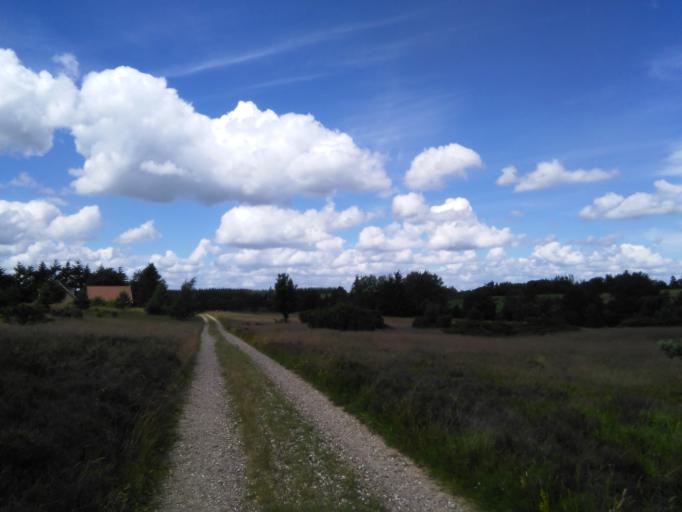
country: DK
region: Central Jutland
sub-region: Silkeborg Kommune
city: Virklund
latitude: 56.0849
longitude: 9.4368
